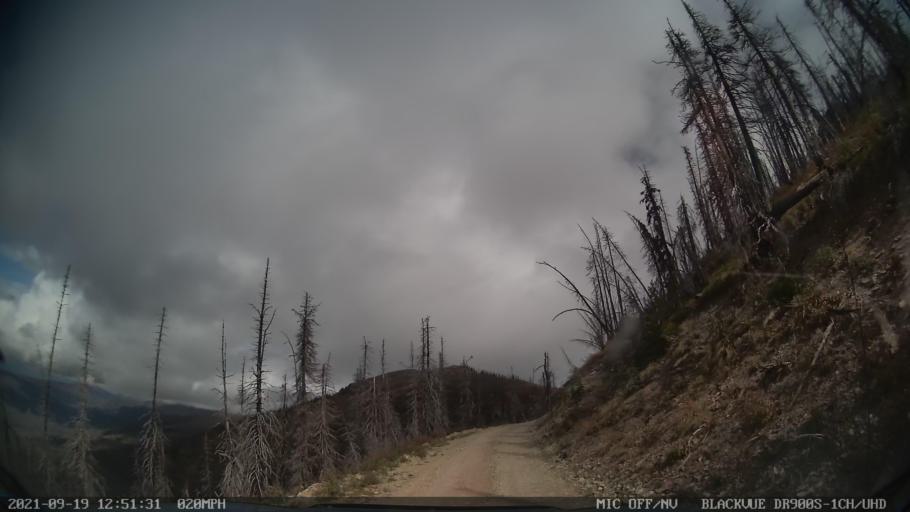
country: US
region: Montana
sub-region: Missoula County
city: Seeley Lake
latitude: 47.1898
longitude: -113.3602
